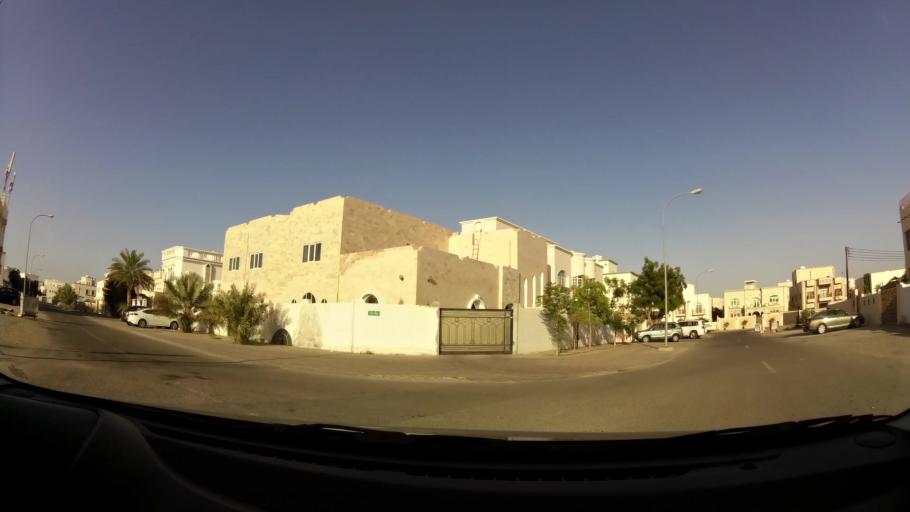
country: OM
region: Muhafazat Masqat
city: As Sib al Jadidah
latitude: 23.6077
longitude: 58.2199
